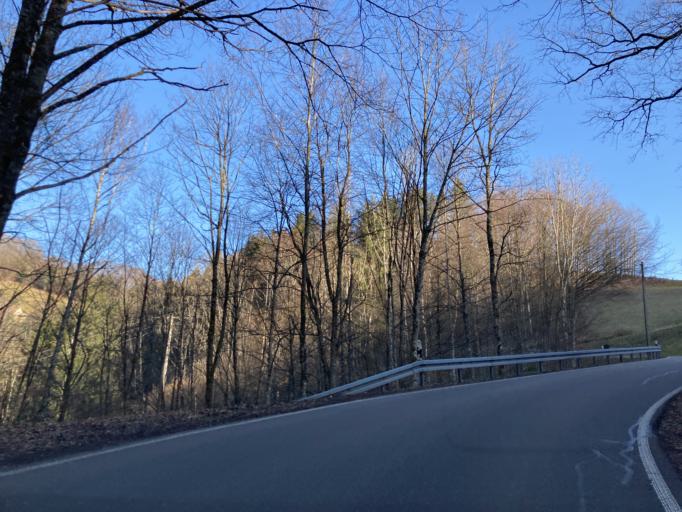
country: DE
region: Baden-Wuerttemberg
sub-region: Freiburg Region
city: Oppenau
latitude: 48.4805
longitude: 8.1966
